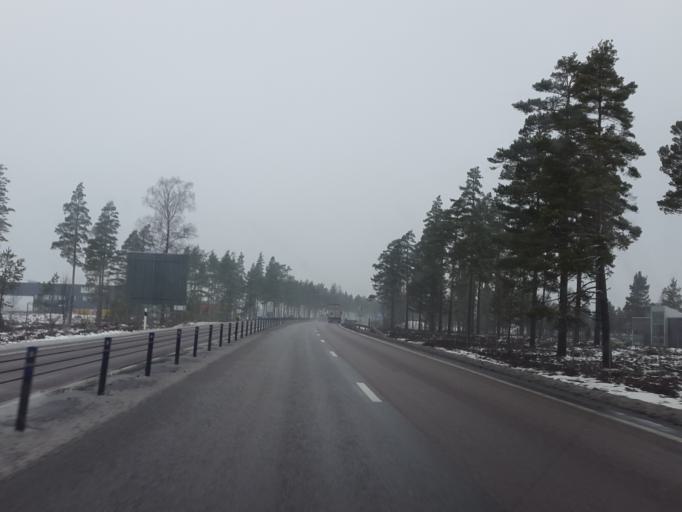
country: SE
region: Joenkoeping
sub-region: Jonkopings Kommun
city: Jonkoping
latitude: 57.7670
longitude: 14.0936
